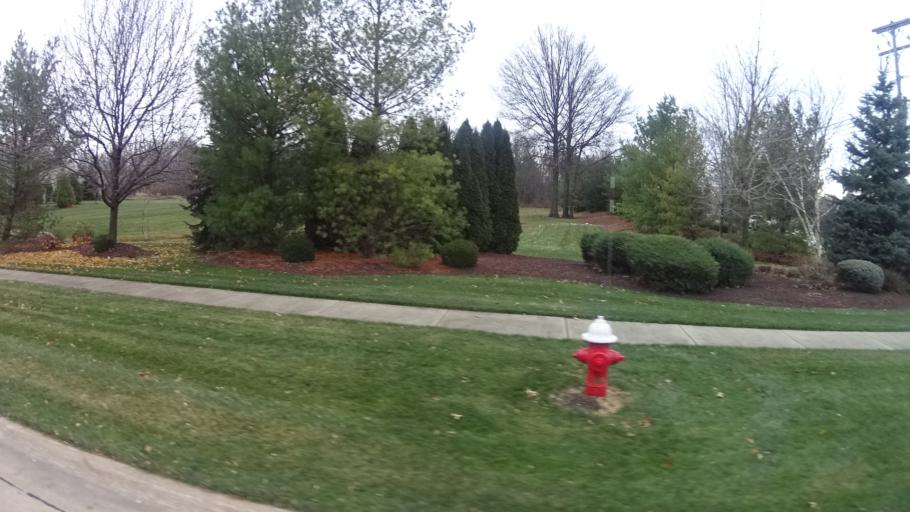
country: US
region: Ohio
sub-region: Lorain County
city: Eaton Estates
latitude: 41.3537
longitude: -81.9809
